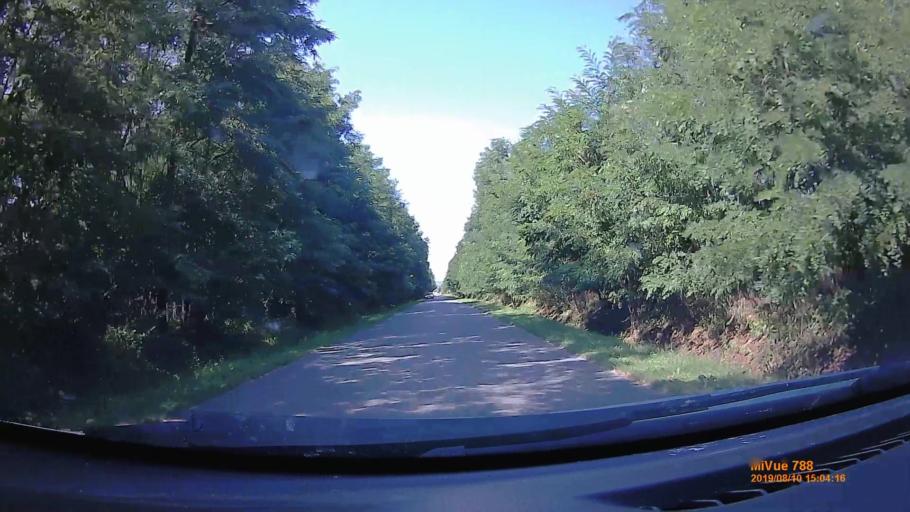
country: HU
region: Somogy
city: Lengyeltoti
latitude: 46.6735
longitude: 17.5670
